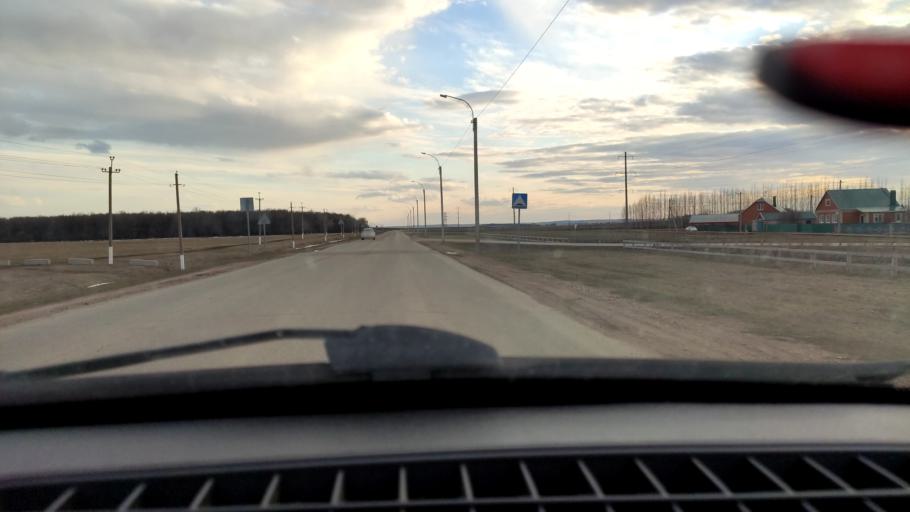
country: RU
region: Bashkortostan
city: Tolbazy
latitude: 54.0016
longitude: 55.8586
